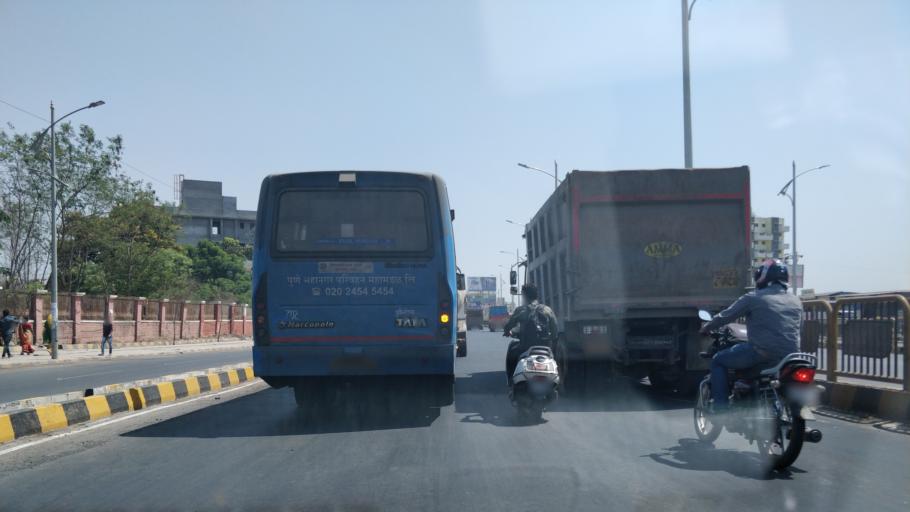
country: IN
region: Maharashtra
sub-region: Pune Division
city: Alandi
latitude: 18.6648
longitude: 73.8875
